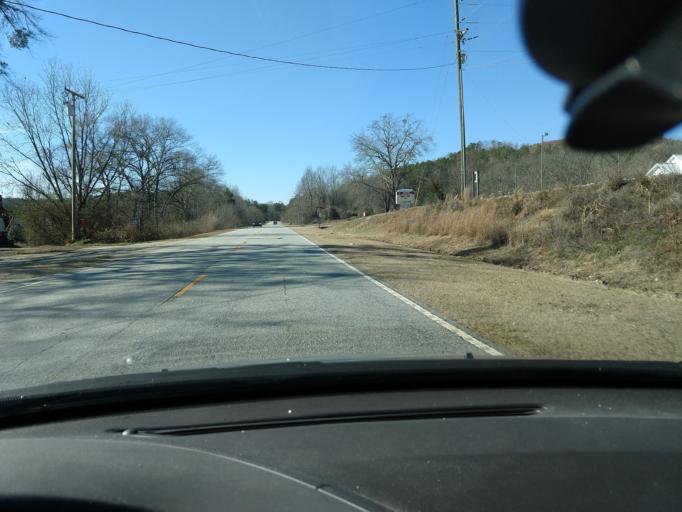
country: US
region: South Carolina
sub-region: Oconee County
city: Westminster
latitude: 34.6127
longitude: -83.1949
